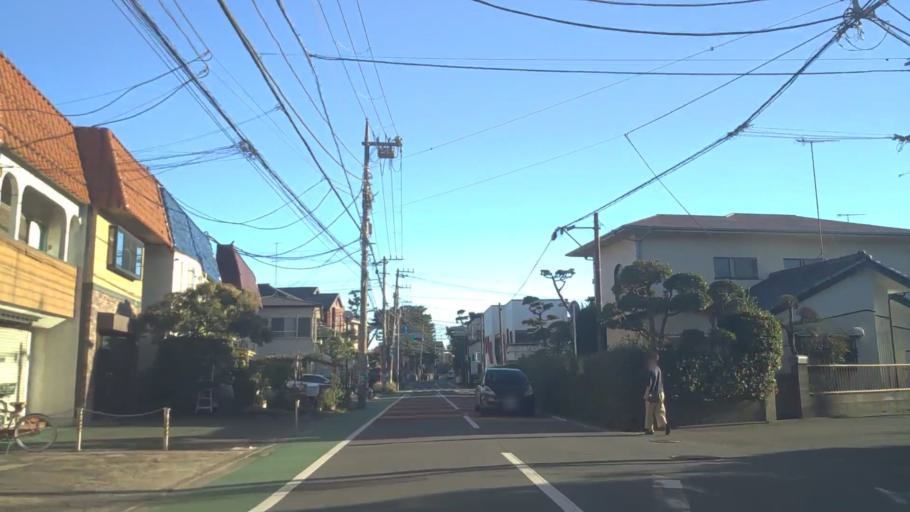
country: JP
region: Kanagawa
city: Chigasaki
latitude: 35.3232
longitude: 139.4152
